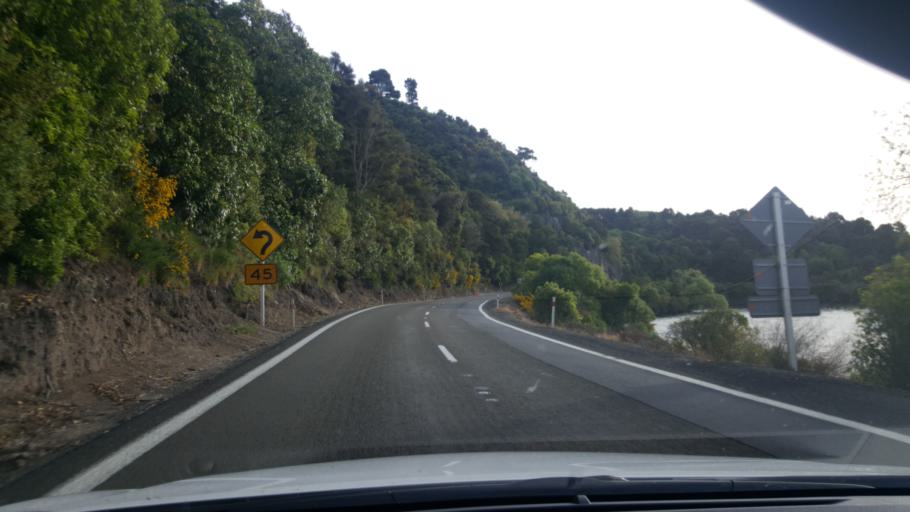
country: NZ
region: Waikato
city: Turangi
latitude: -38.8816
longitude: 175.9707
